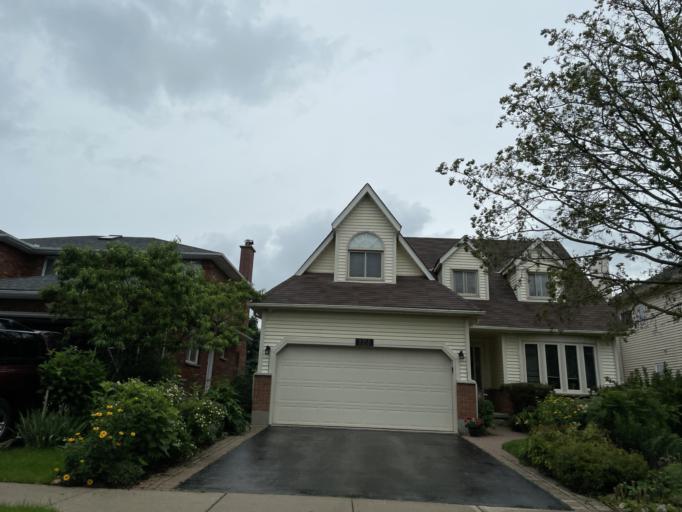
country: CA
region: Ontario
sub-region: Wellington County
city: Guelph
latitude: 43.5252
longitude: -80.2535
